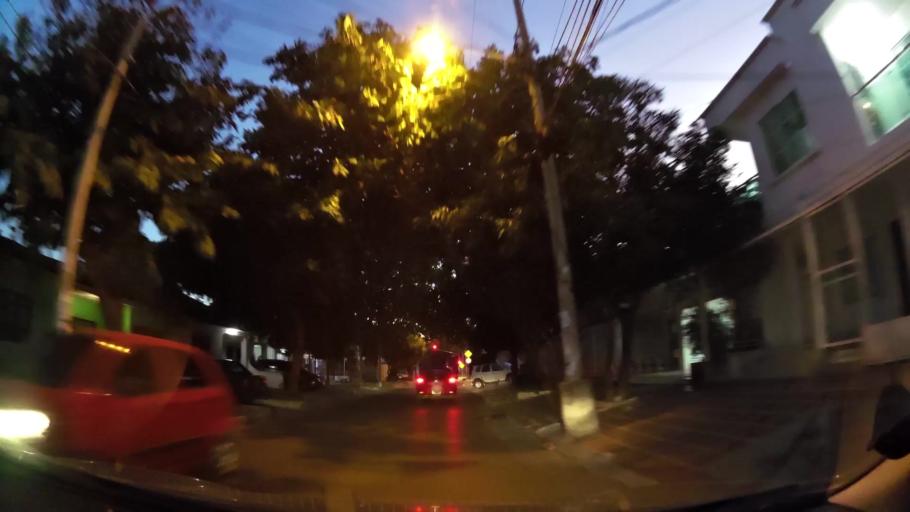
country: CO
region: Atlantico
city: Barranquilla
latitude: 10.9763
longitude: -74.8029
